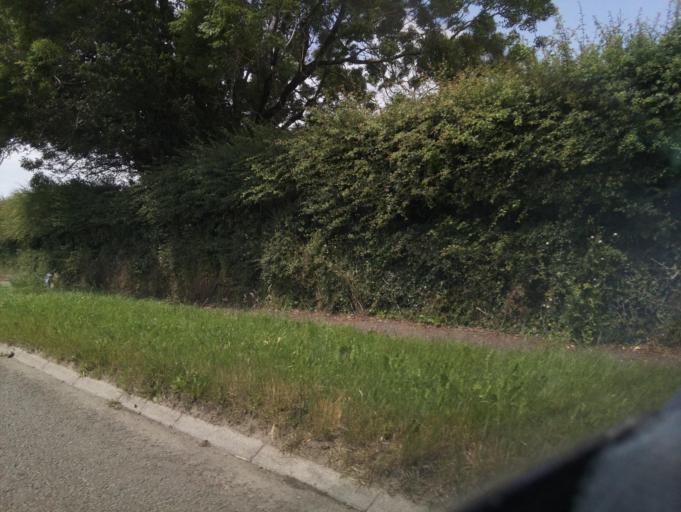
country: GB
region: Wales
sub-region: Vale of Glamorgan
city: Rhoose
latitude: 51.4568
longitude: -3.3620
